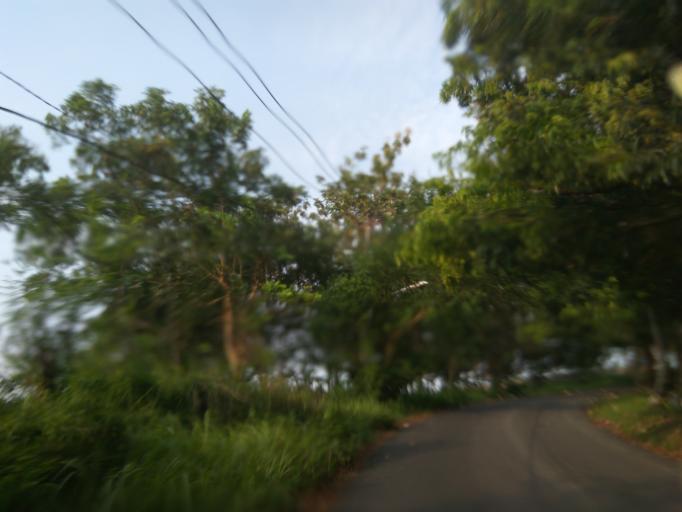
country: ID
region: Central Java
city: Semarang
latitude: -7.0164
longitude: 110.3987
